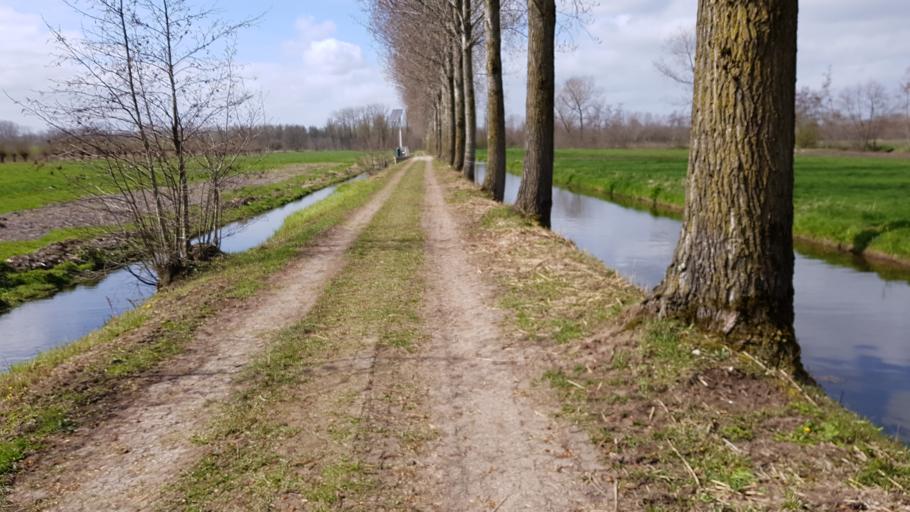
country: NL
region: Utrecht
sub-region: Gemeente IJsselstein
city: IJsselstein
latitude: 51.9600
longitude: 5.0179
